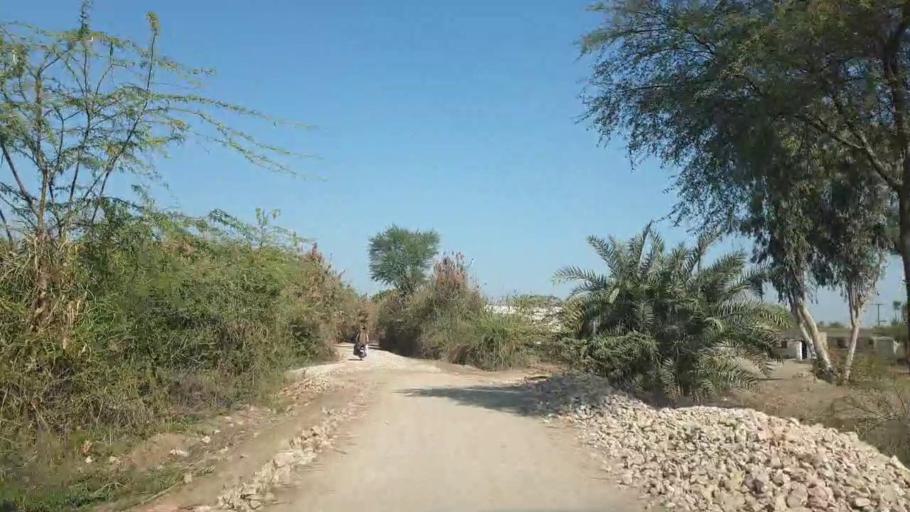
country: PK
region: Sindh
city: Tando Adam
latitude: 25.6424
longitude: 68.7117
